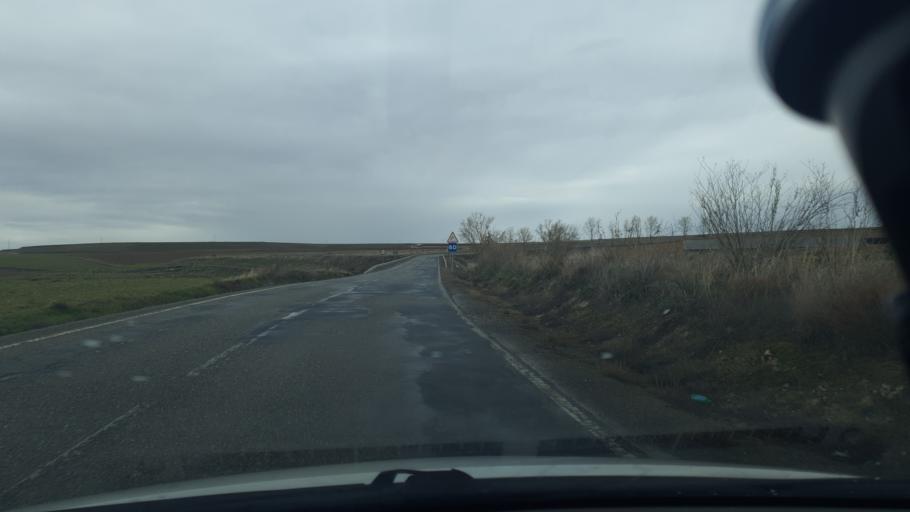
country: ES
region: Castille and Leon
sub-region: Provincia de Segovia
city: Segovia
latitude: 40.9648
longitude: -4.1389
